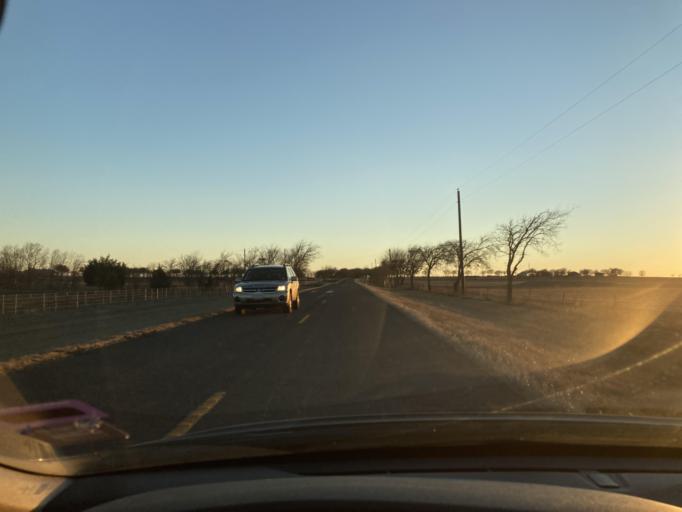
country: US
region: Texas
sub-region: Ellis County
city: Nash
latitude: 32.3106
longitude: -96.8833
